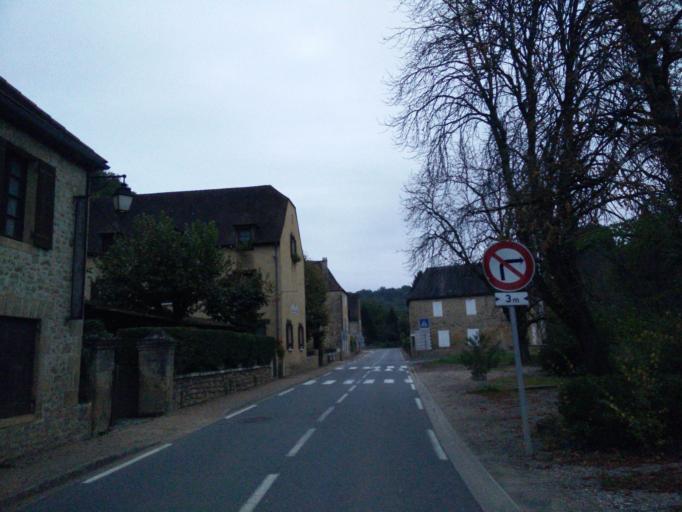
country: FR
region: Aquitaine
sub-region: Departement de la Dordogne
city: Carsac-Aillac
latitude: 44.8189
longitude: 1.2923
